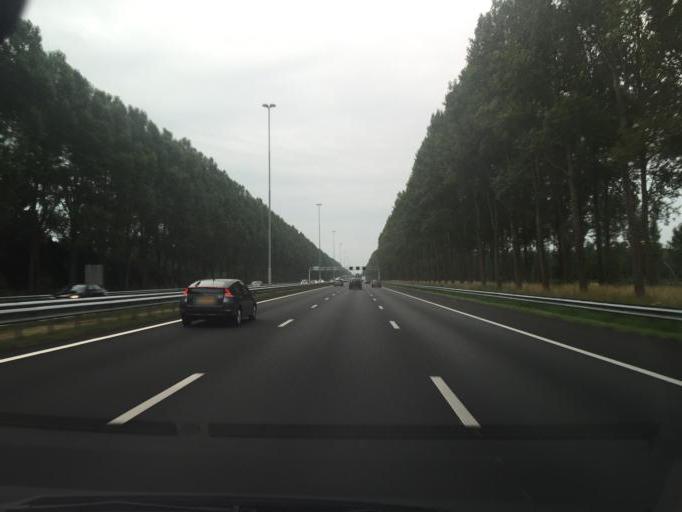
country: NL
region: North Brabant
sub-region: Gemeente Best
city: Best
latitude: 51.5494
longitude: 5.3668
